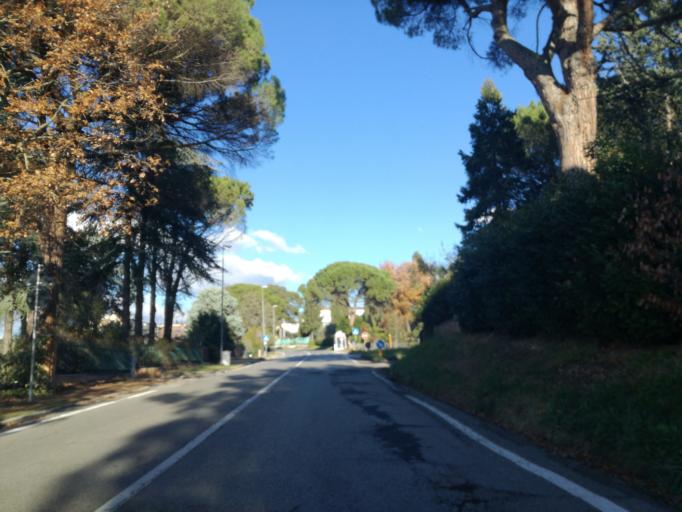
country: IT
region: Umbria
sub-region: Provincia di Perugia
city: Perugia
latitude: 43.0775
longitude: 12.3987
